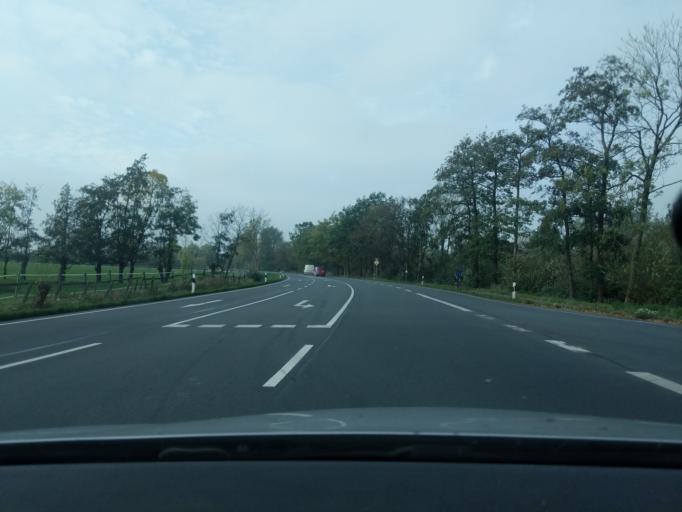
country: DE
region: Lower Saxony
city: Neuhaus an der Oste
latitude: 53.7970
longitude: 9.0494
